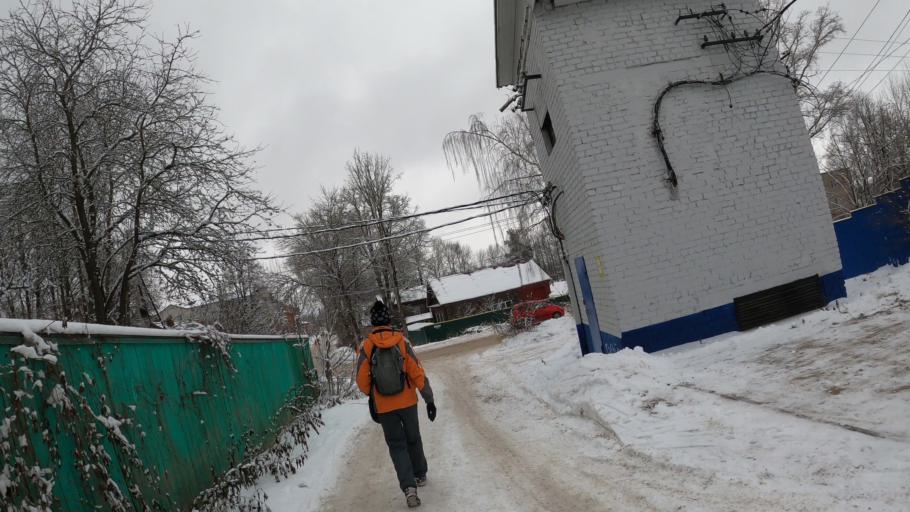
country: RU
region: Jaroslavl
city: Pereslavl'-Zalesskiy
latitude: 56.7446
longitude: 38.8624
